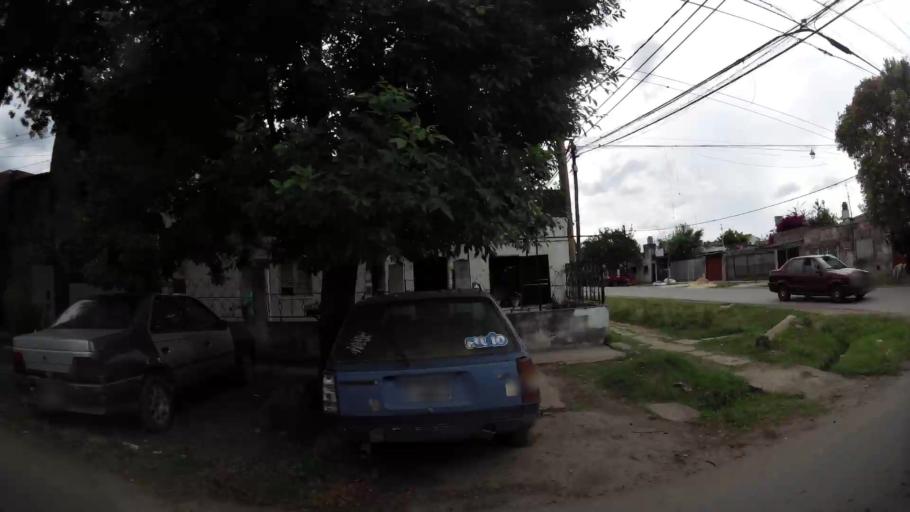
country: AR
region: Santa Fe
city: Gobernador Galvez
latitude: -33.0121
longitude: -60.6542
